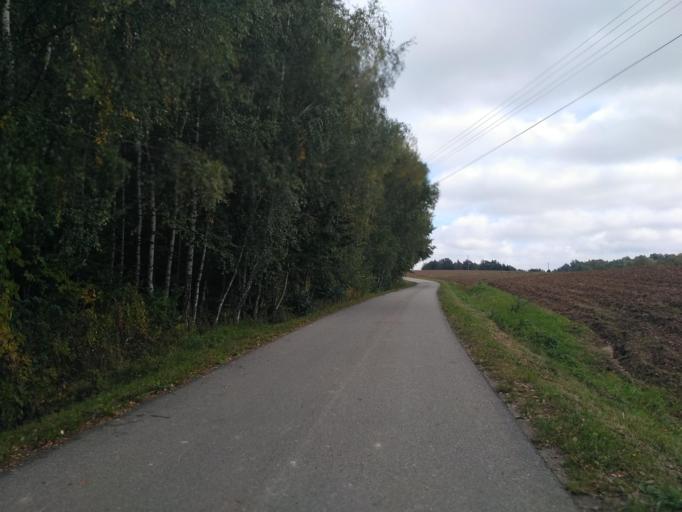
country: PL
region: Subcarpathian Voivodeship
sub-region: Powiat ropczycko-sedziszowski
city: Niedzwiada
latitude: 49.9200
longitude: 21.4981
